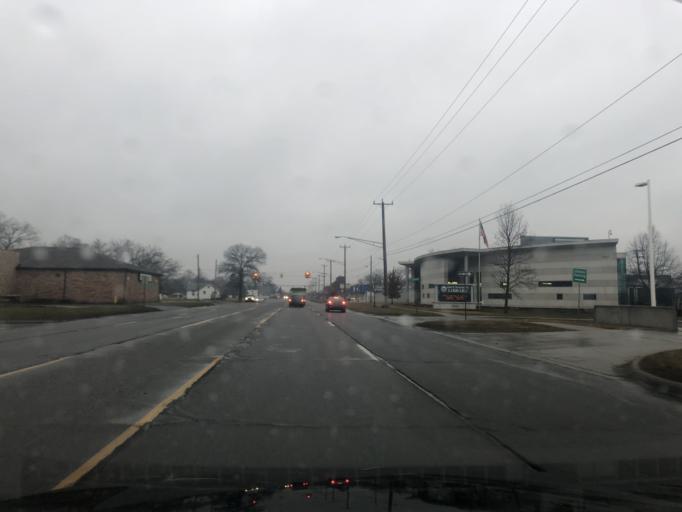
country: US
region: Michigan
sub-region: Wayne County
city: Taylor
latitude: 42.2690
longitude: -83.2748
